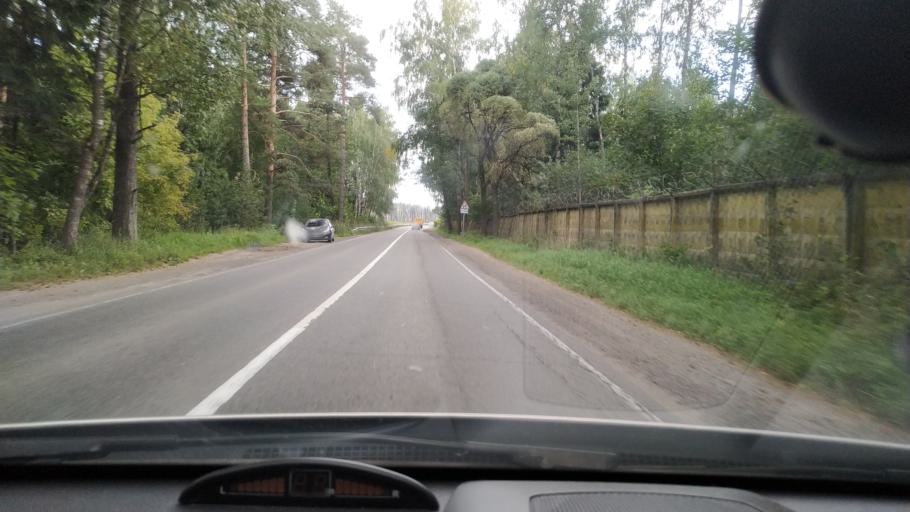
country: RU
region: Moskovskaya
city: Chornaya
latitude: 55.7754
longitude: 38.0494
